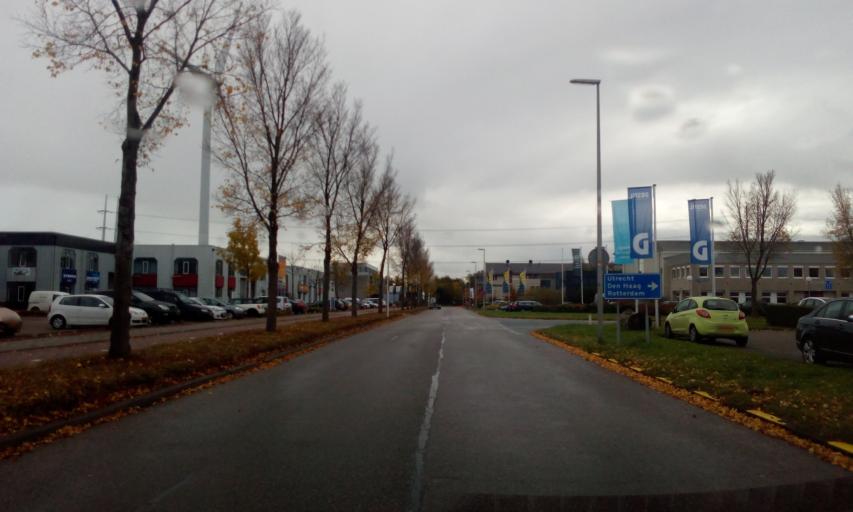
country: NL
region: South Holland
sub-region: Gemeente Zoetermeer
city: Zoetermeer
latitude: 52.0378
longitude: 4.5063
